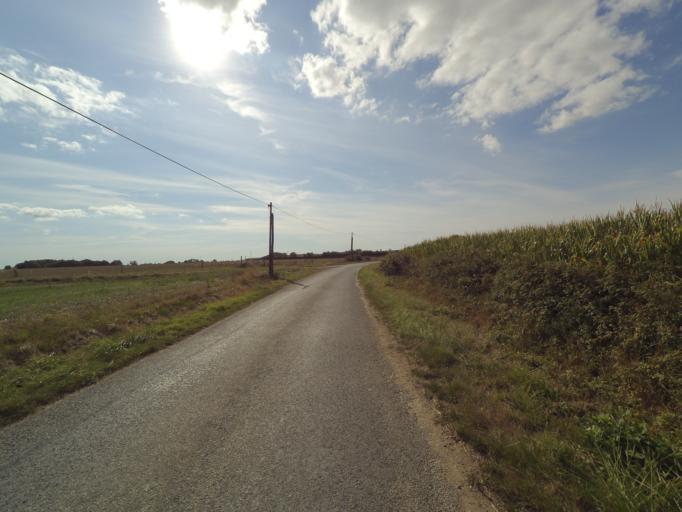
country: FR
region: Pays de la Loire
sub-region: Departement de la Loire-Atlantique
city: Vieillevigne
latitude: 46.9846
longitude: -1.3907
